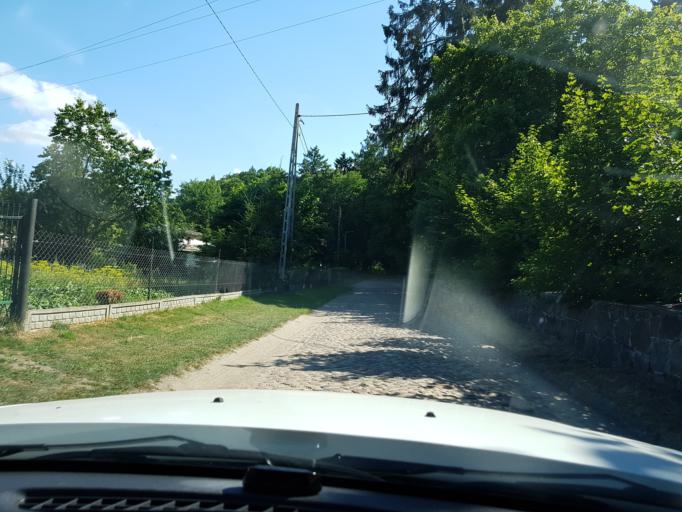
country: PL
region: West Pomeranian Voivodeship
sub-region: Powiat bialogardzki
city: Karlino
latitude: 53.9331
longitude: 15.8270
